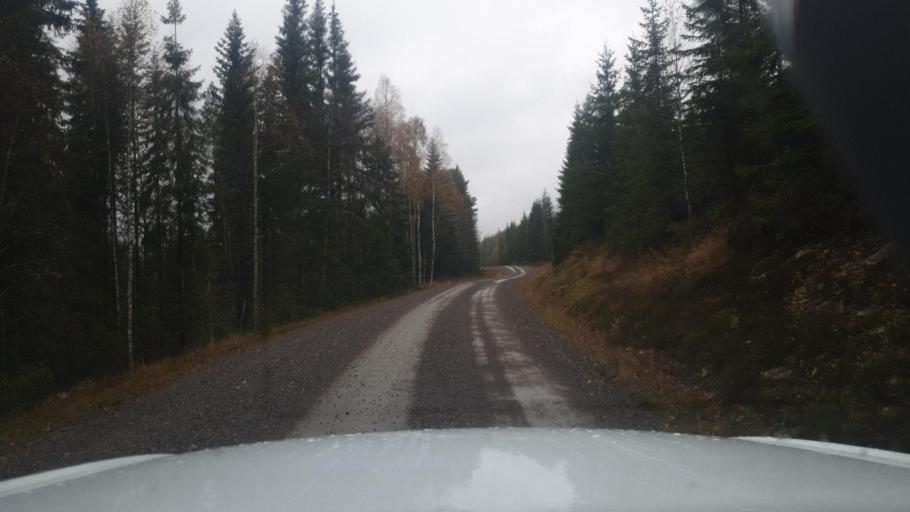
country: SE
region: Vaermland
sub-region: Eda Kommun
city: Charlottenberg
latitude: 60.0974
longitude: 12.6103
